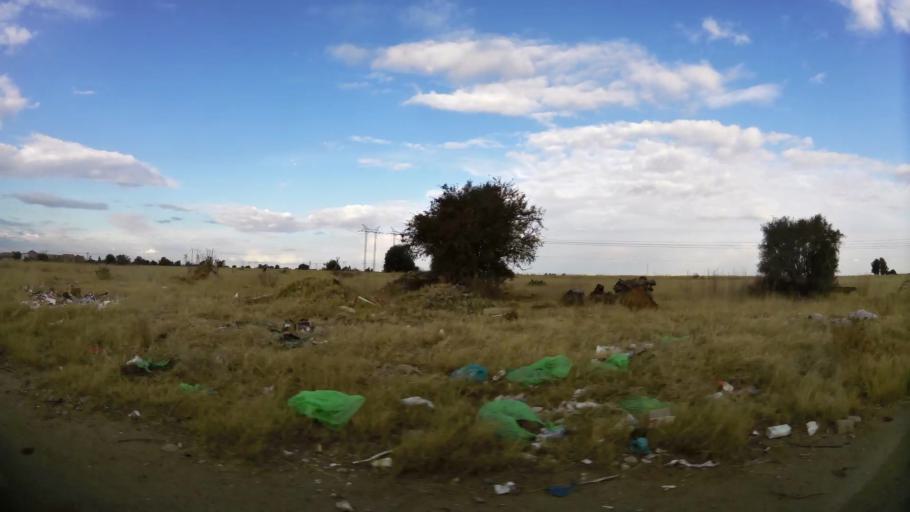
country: ZA
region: Orange Free State
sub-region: Lejweleputswa District Municipality
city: Welkom
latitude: -28.0061
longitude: 26.7321
